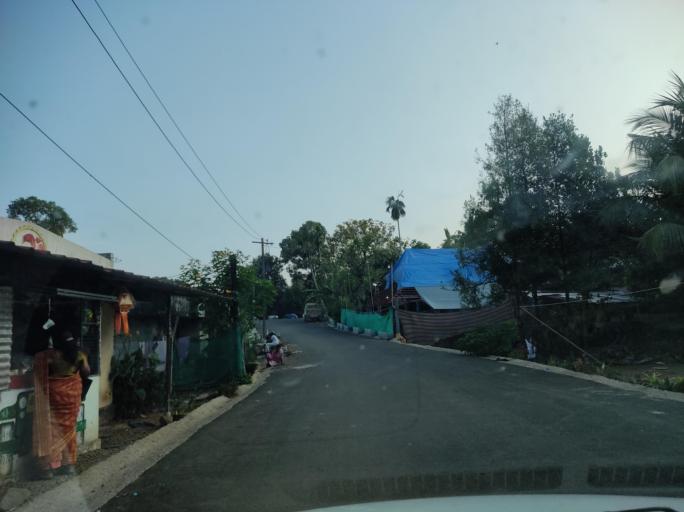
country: IN
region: Kerala
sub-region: Pattanamtitta
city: Tiruvalla
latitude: 9.3605
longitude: 76.5663
